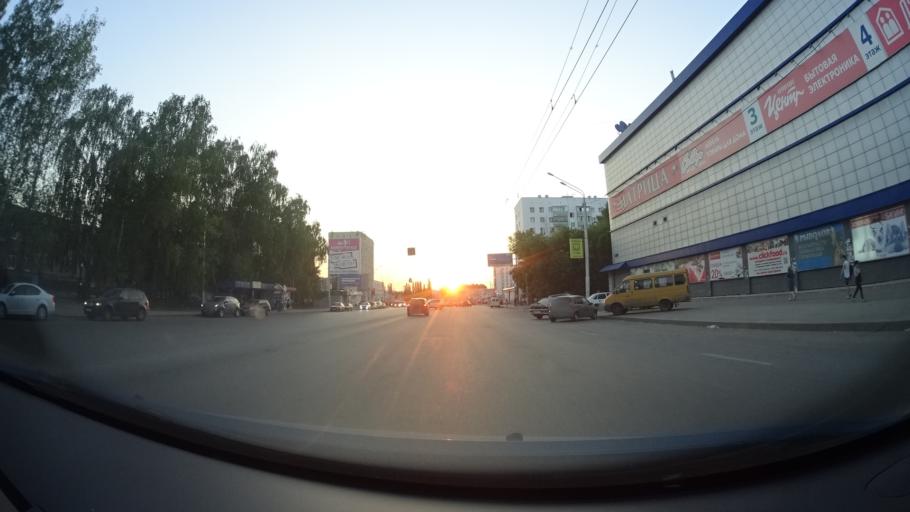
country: RU
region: Bashkortostan
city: Ufa
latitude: 54.7489
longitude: 55.9878
